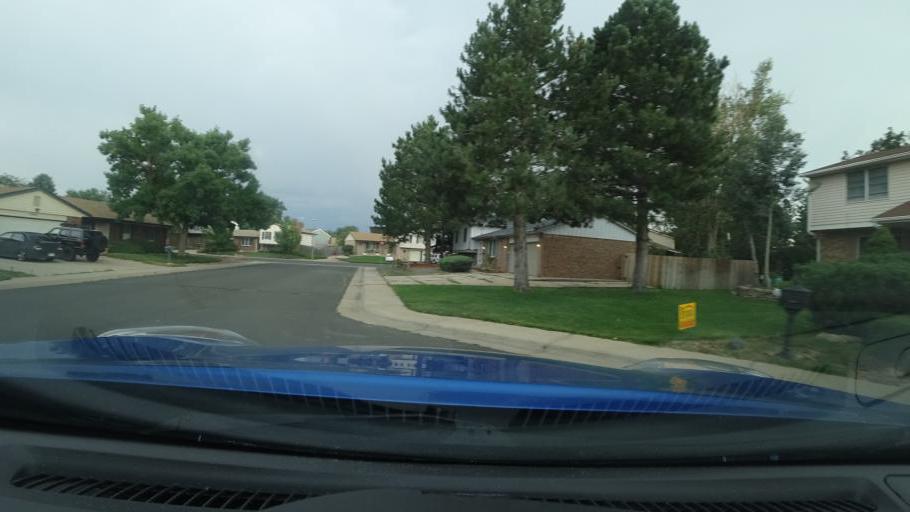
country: US
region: Colorado
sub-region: Adams County
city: Aurora
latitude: 39.6922
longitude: -104.8255
